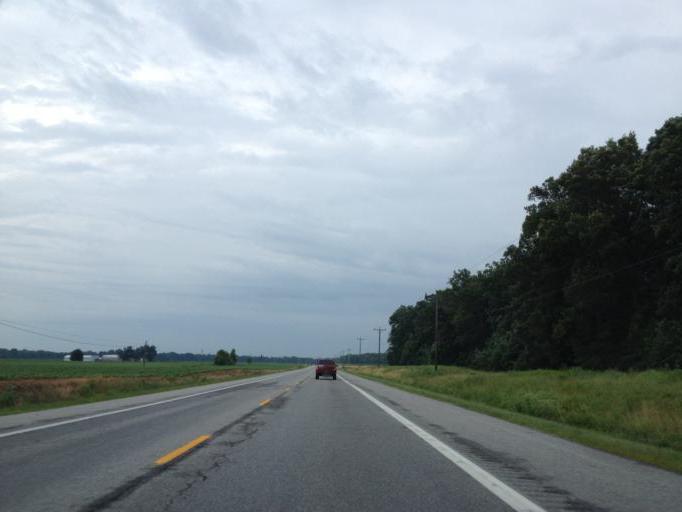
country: US
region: Maryland
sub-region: Caroline County
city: Ridgely
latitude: 38.9285
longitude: -76.0045
